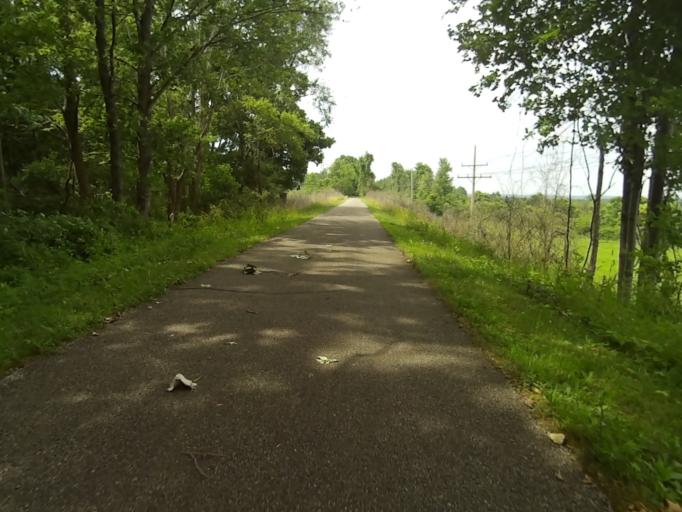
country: US
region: Ohio
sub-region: Cuyahoga County
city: Walton Hills
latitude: 41.3543
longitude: -81.5695
